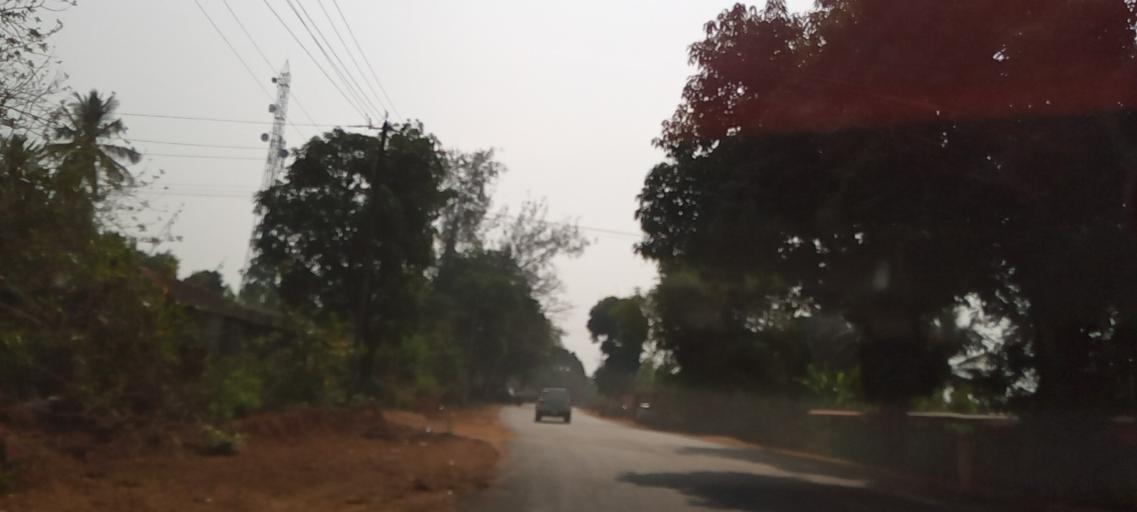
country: IN
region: Karnataka
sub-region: Udupi
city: Someshwar
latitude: 13.5285
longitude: 74.9216
